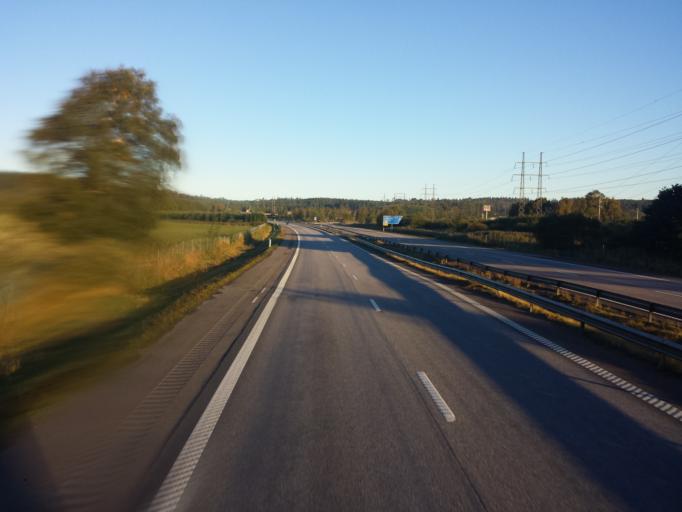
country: SE
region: Halland
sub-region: Kungsbacka Kommun
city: Kungsbacka
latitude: 57.4684
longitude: 12.0665
